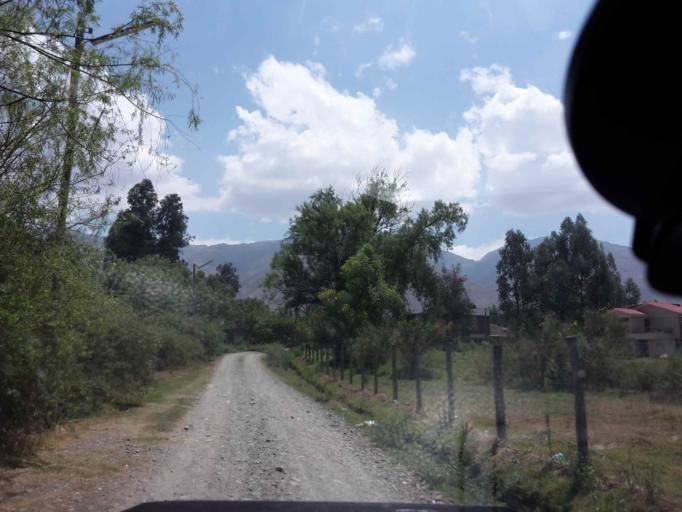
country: BO
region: Cochabamba
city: Cochabamba
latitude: -17.3515
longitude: -66.2147
